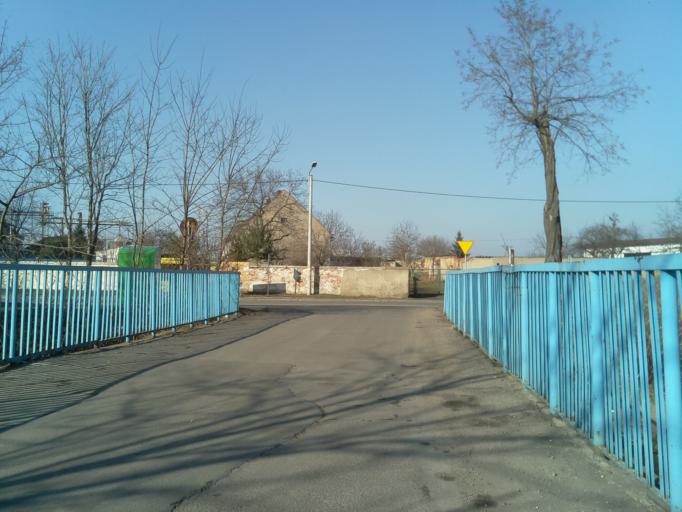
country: PL
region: Lower Silesian Voivodeship
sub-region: Powiat swidnicki
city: Swiebodzice
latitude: 50.8687
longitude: 16.3335
